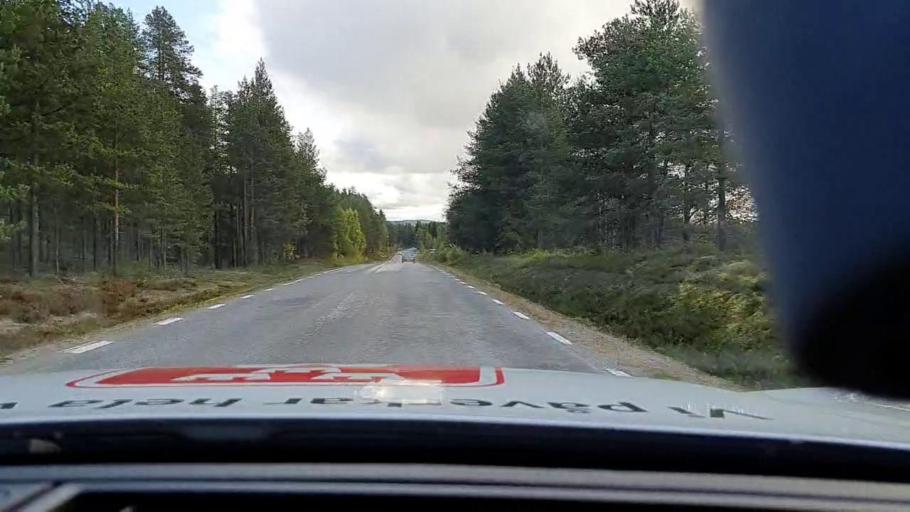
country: SE
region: Vaesterbotten
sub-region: Skelleftea Kommun
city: Langsele
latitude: 64.9593
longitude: 19.9023
